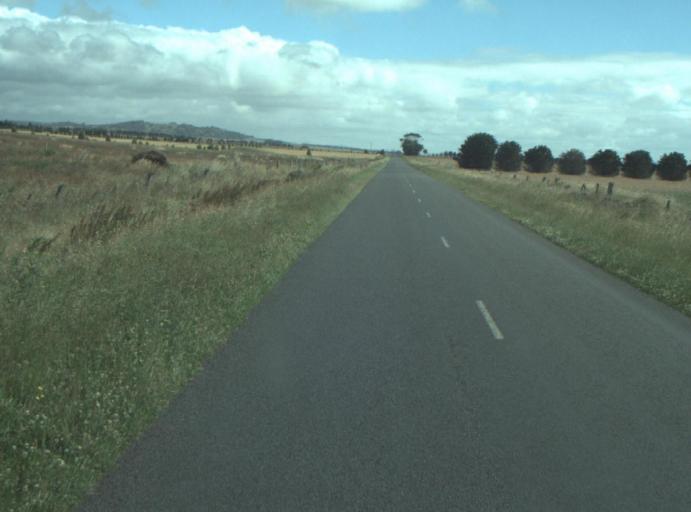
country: AU
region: Victoria
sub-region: Greater Geelong
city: Lara
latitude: -37.9326
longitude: 144.3113
